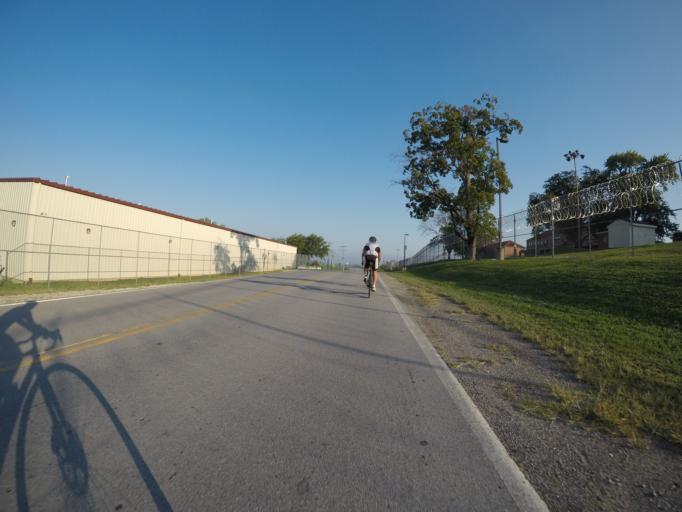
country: US
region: Kansas
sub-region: Leavenworth County
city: Lansing
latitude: 39.2540
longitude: -94.8789
